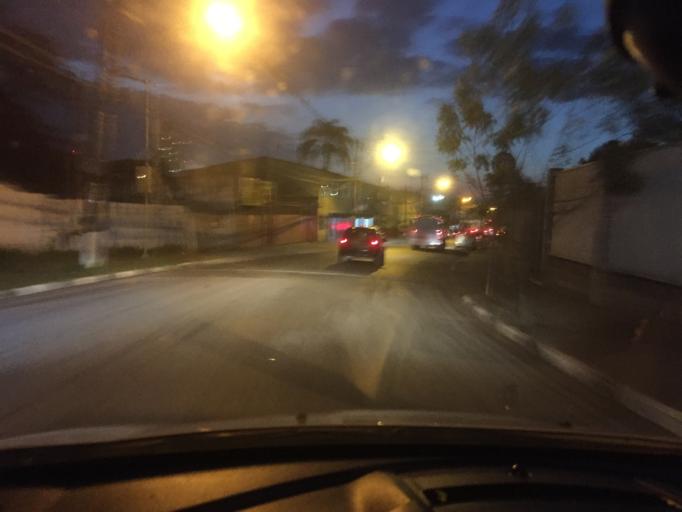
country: BR
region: Sao Paulo
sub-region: Campo Limpo Paulista
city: Campo Limpo Paulista
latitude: -23.2065
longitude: -46.7814
